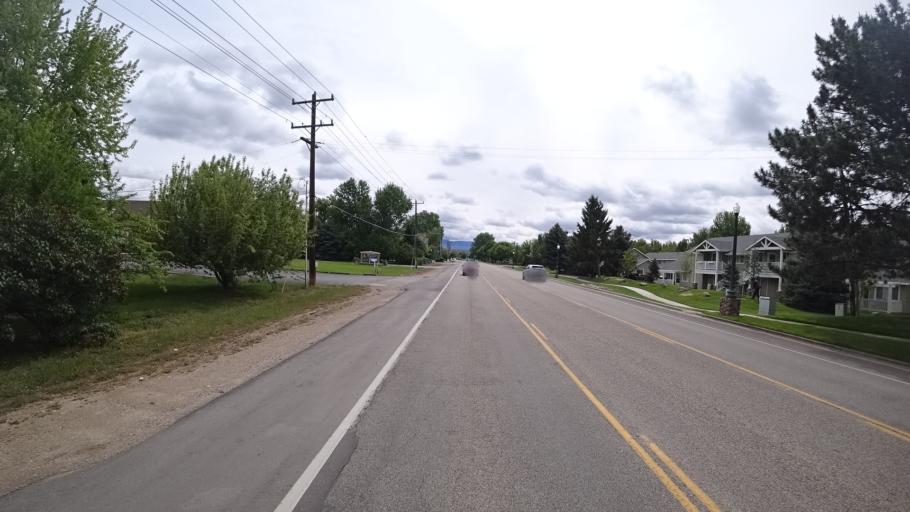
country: US
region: Idaho
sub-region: Ada County
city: Eagle
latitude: 43.6953
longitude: -116.3617
